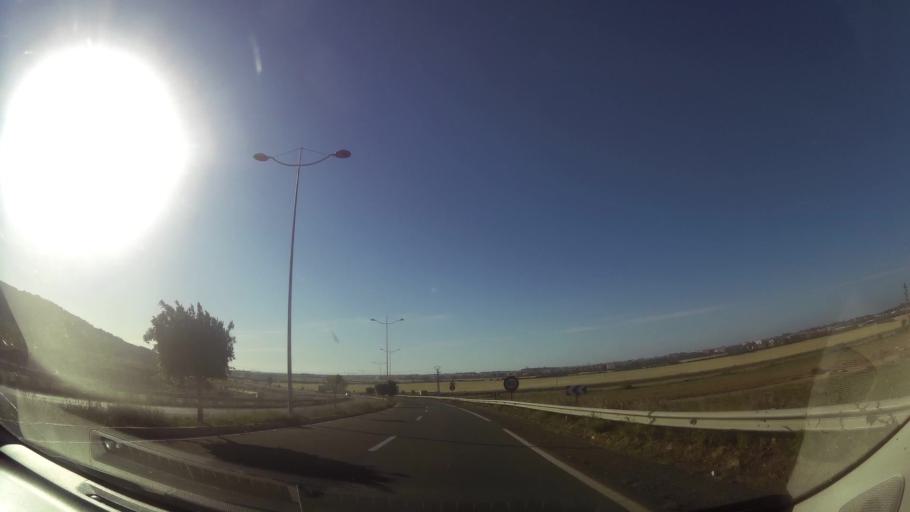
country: MA
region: Oriental
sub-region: Berkane-Taourirt
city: Madagh
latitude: 35.0626
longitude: -2.2246
